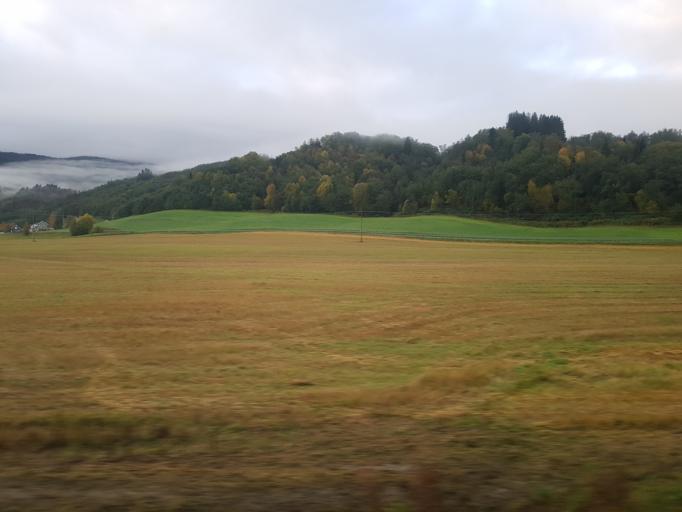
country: NO
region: Sor-Trondelag
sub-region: Melhus
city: Melhus
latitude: 63.2963
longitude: 10.2867
